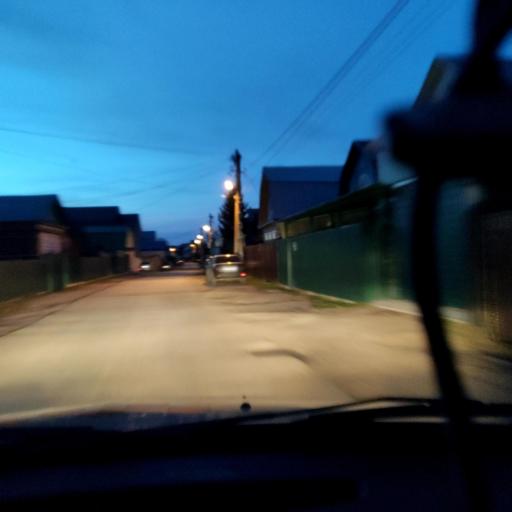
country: RU
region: Bashkortostan
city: Ufa
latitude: 54.7263
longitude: 55.9029
